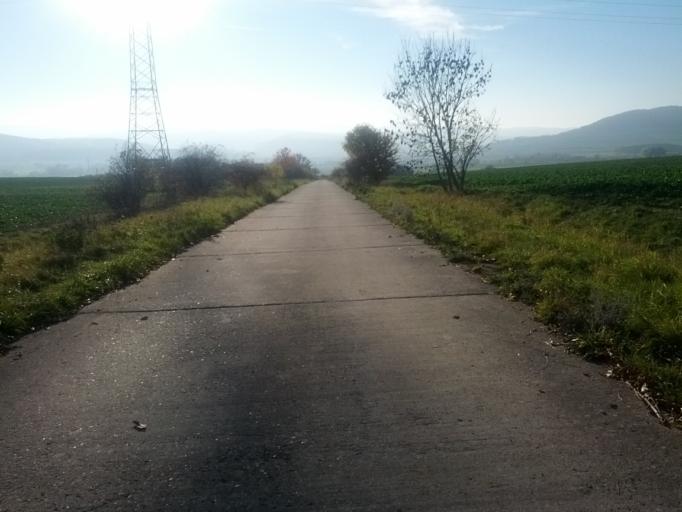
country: DE
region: Thuringia
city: Mechterstadt
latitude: 50.9567
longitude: 10.5262
